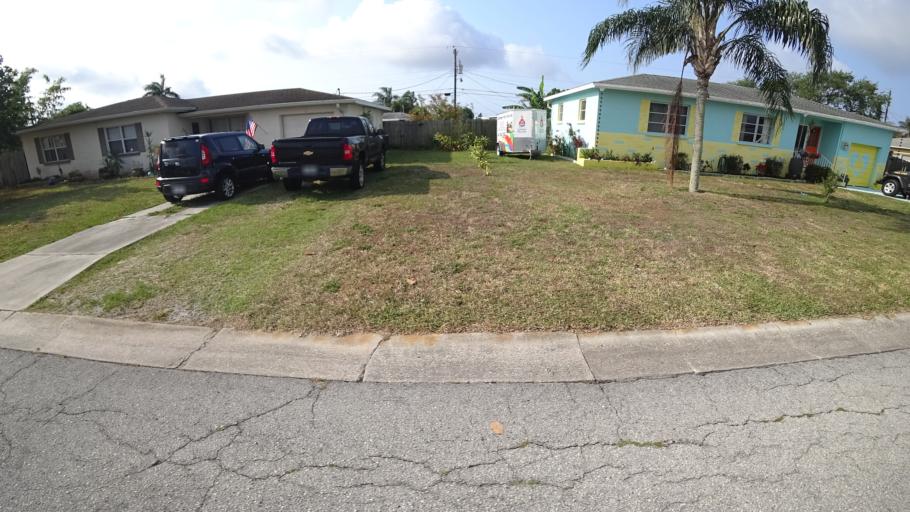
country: US
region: Florida
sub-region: Manatee County
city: South Bradenton
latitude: 27.4576
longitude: -82.5719
